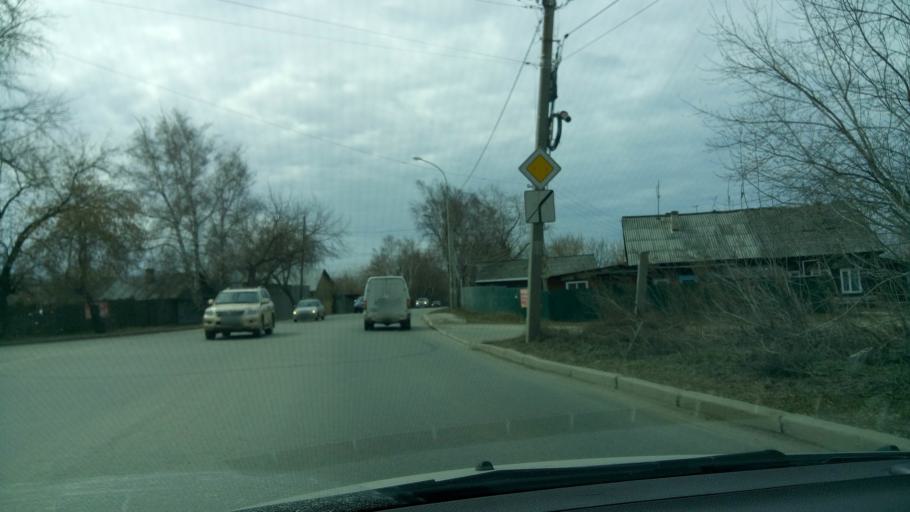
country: RU
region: Sverdlovsk
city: Yekaterinburg
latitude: 56.8835
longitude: 60.7048
